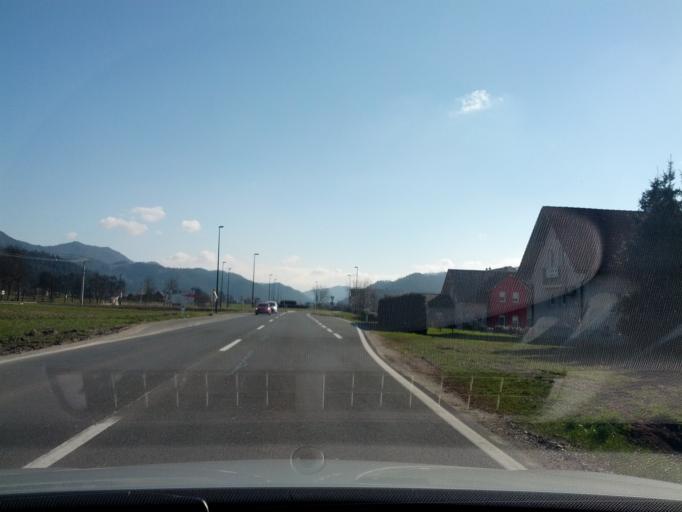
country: SI
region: Dol pri Ljubljani
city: Dol pri Ljubljani
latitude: 46.0898
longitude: 14.6374
